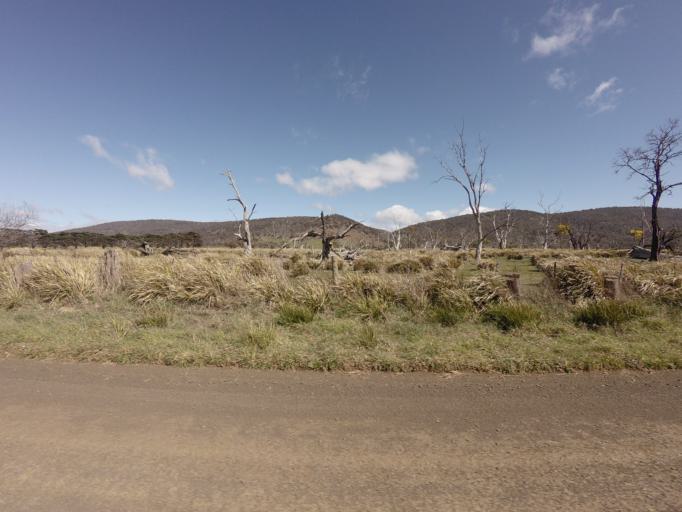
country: AU
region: Tasmania
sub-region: Northern Midlands
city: Evandale
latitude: -41.9480
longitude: 147.4331
